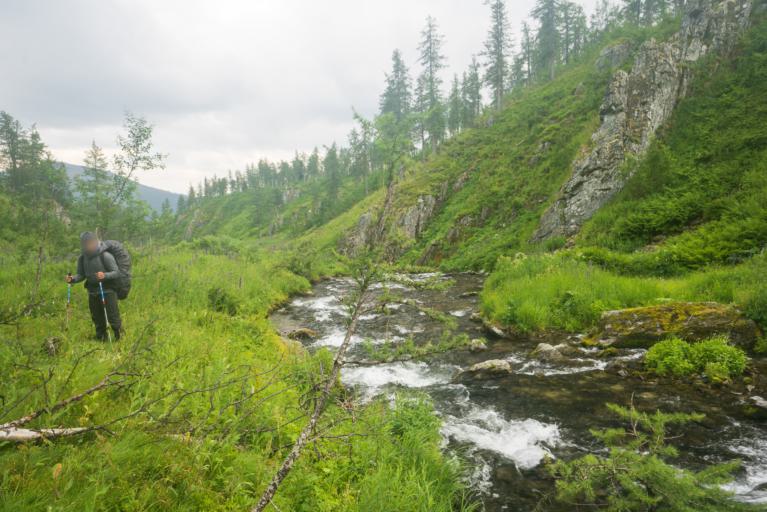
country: RU
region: Komi Republic
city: Synya
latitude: 64.7881
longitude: 58.9646
